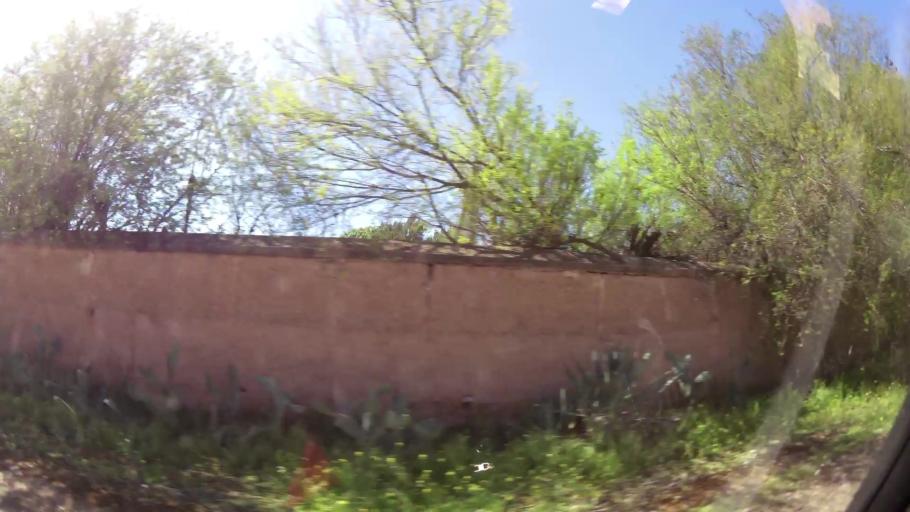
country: MA
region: Marrakech-Tensift-Al Haouz
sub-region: Marrakech
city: Marrakesh
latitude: 31.6654
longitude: -7.9593
